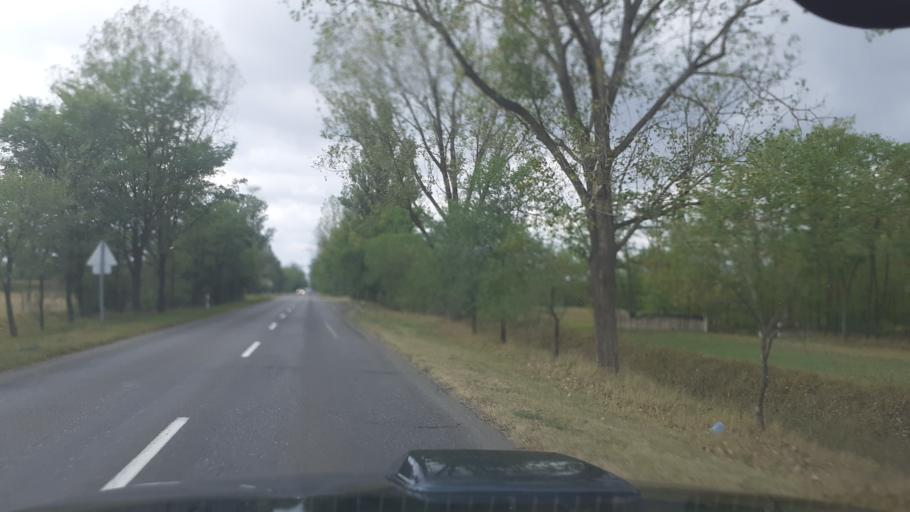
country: HU
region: Bacs-Kiskun
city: Agasegyhaza
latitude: 46.8781
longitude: 19.4905
